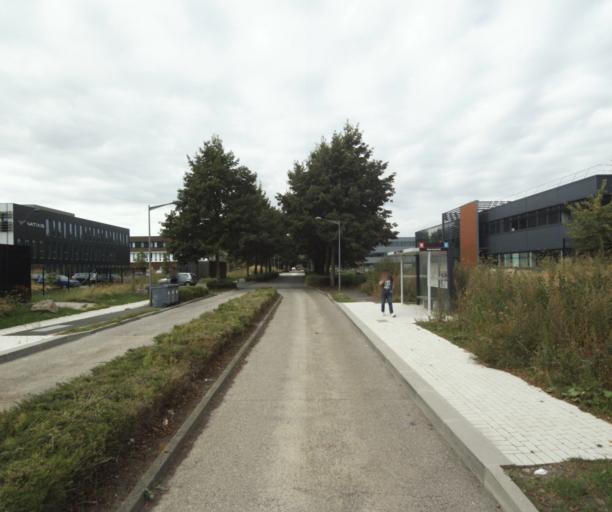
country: FR
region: Nord-Pas-de-Calais
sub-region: Departement du Nord
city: Villeneuve-d'Ascq
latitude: 50.6030
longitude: 3.1534
